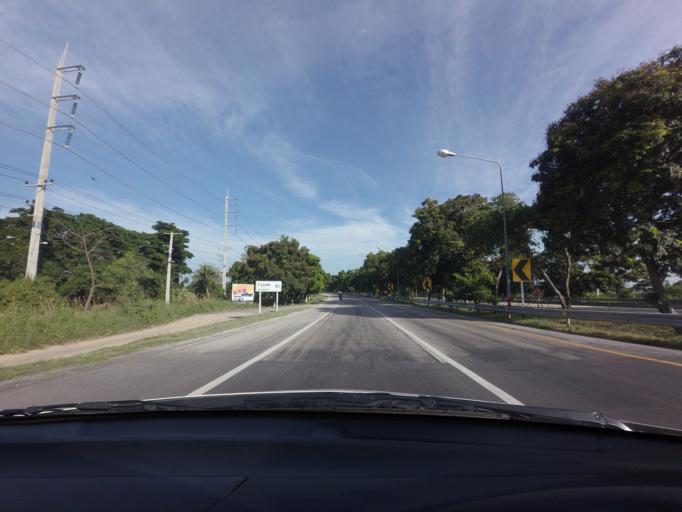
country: TH
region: Suphan Buri
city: Bang Pla Ma
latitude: 14.3442
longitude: 100.1903
